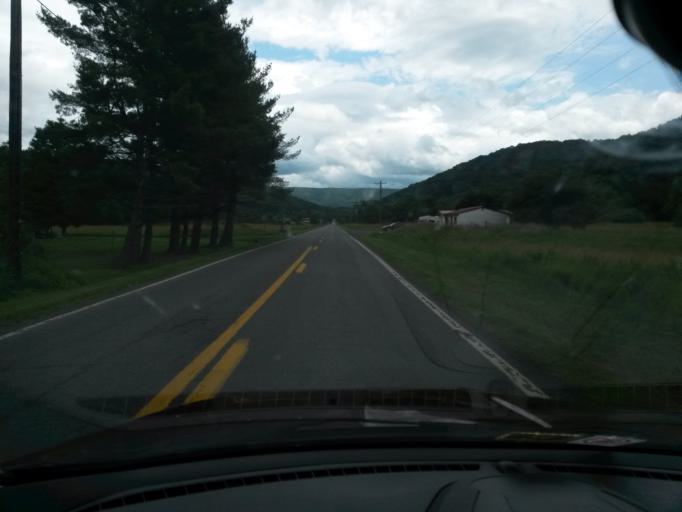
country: US
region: West Virginia
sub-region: Monroe County
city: Union
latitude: 37.5743
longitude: -80.4199
